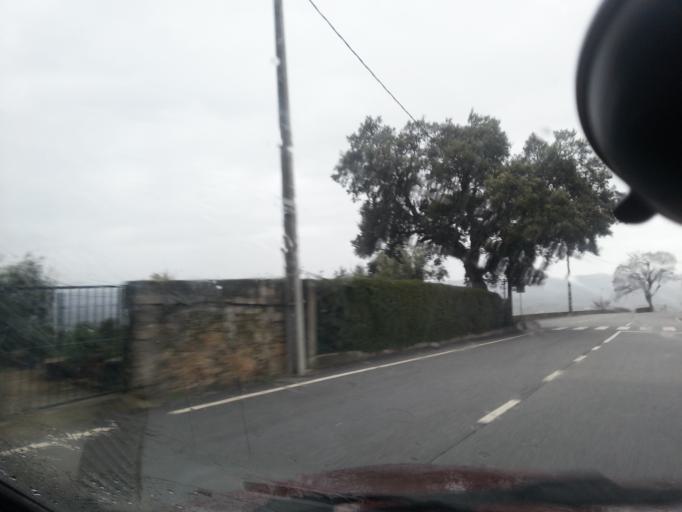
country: PT
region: Guarda
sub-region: Manteigas
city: Manteigas
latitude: 40.4972
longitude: -7.5921
